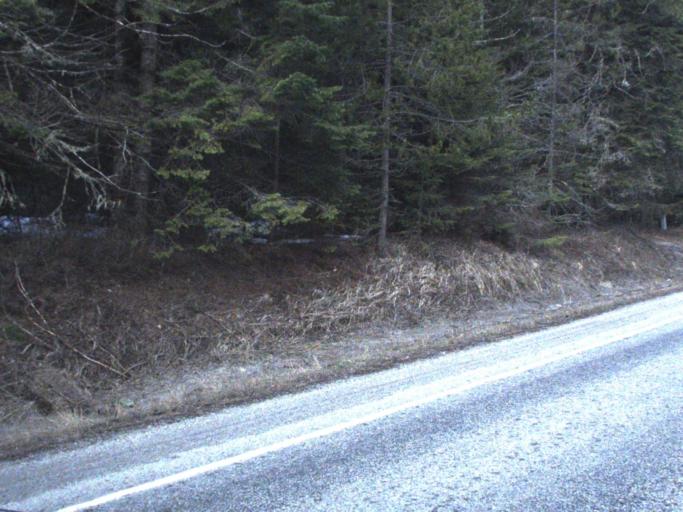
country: US
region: Washington
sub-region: Stevens County
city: Chewelah
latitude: 48.6107
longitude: -117.3648
